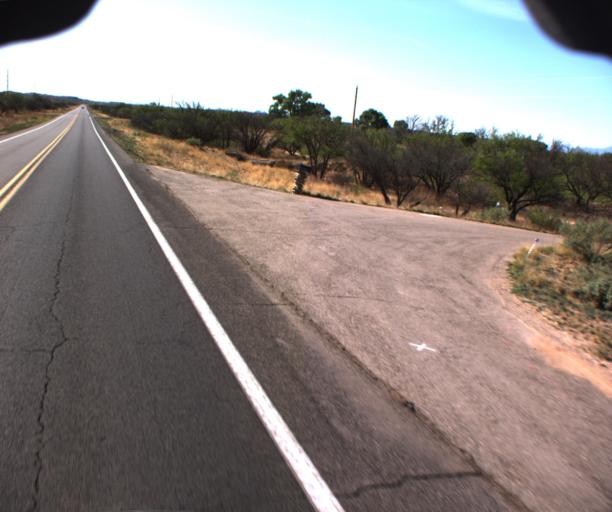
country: US
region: Arizona
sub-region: Cochise County
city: Saint David
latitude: 31.8498
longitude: -110.1981
